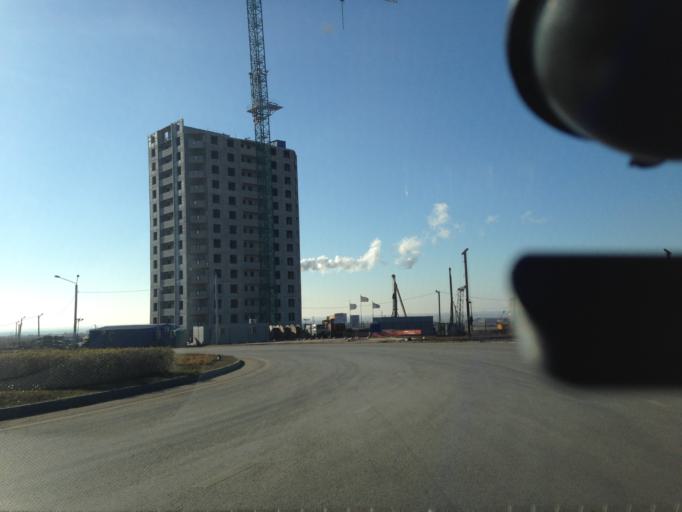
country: RU
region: Rostov
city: Kalinin
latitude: 47.2328
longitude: 39.5890
